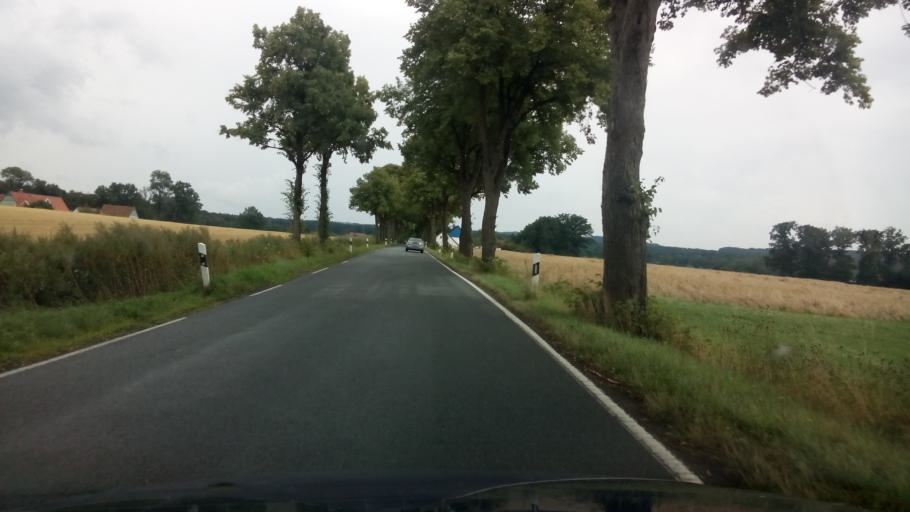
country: DE
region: Lower Saxony
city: Bad Essen
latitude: 52.3014
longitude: 8.3280
